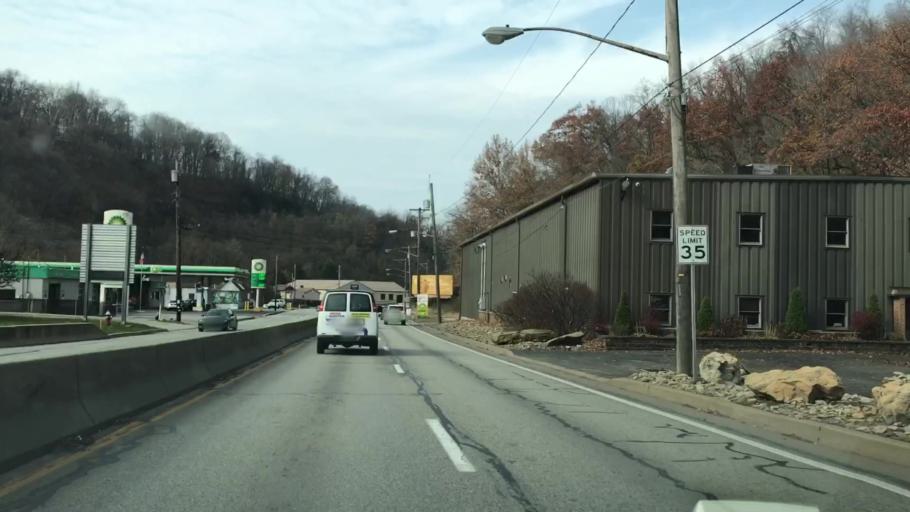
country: US
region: Pennsylvania
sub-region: Allegheny County
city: Green Tree
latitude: 40.4265
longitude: -80.0211
